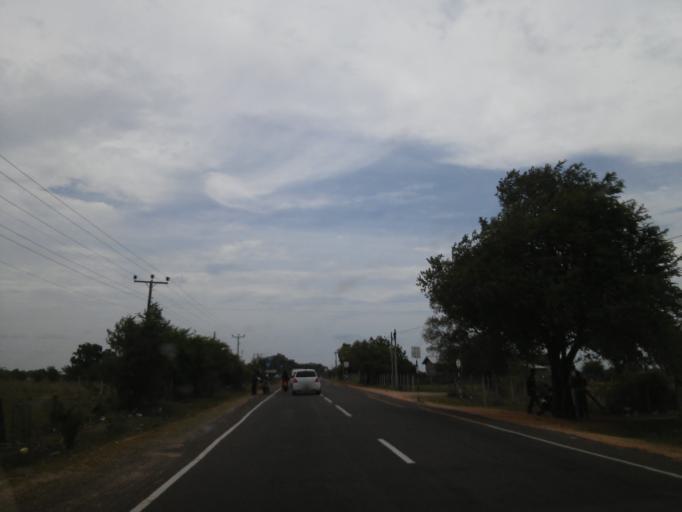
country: LK
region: Eastern Province
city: Trincomalee
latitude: 8.6575
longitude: 81.1995
